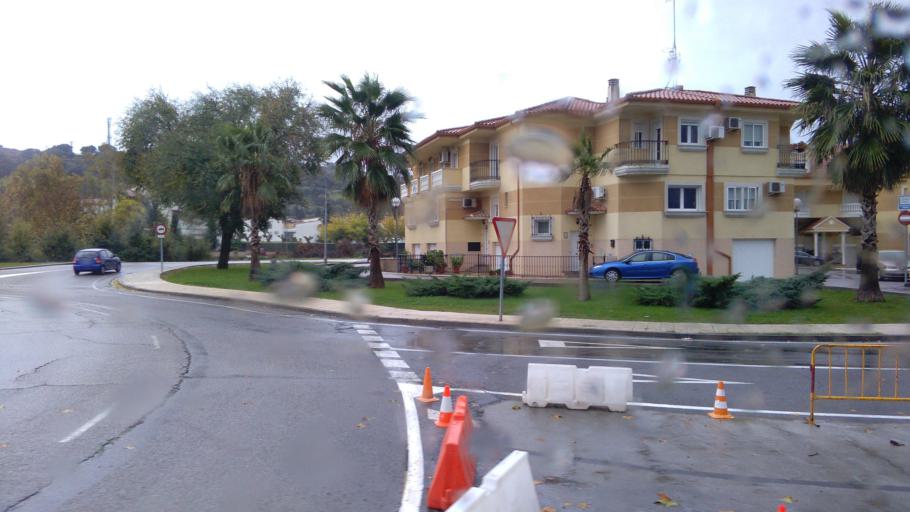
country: ES
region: Extremadura
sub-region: Provincia de Caceres
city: Navalmoral de la Mata
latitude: 39.8922
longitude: -5.5297
